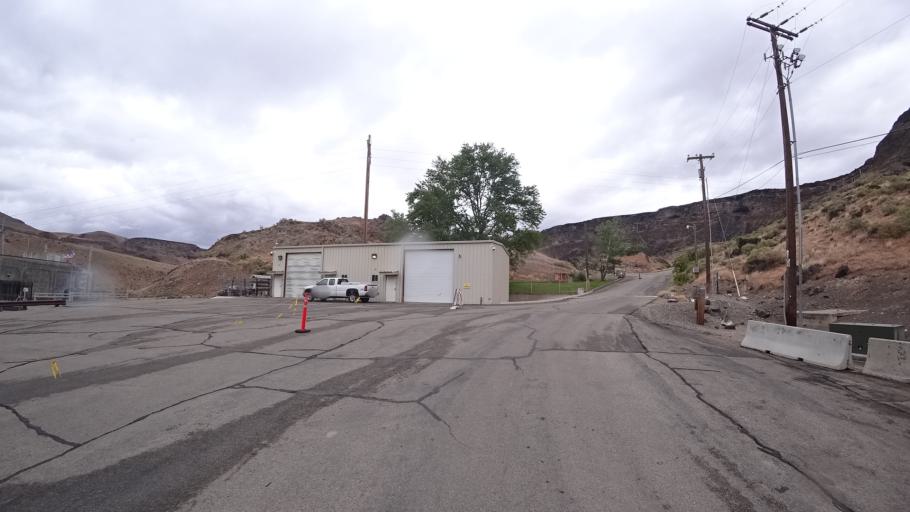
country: US
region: Idaho
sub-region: Owyhee County
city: Murphy
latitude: 43.2439
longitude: -116.3772
